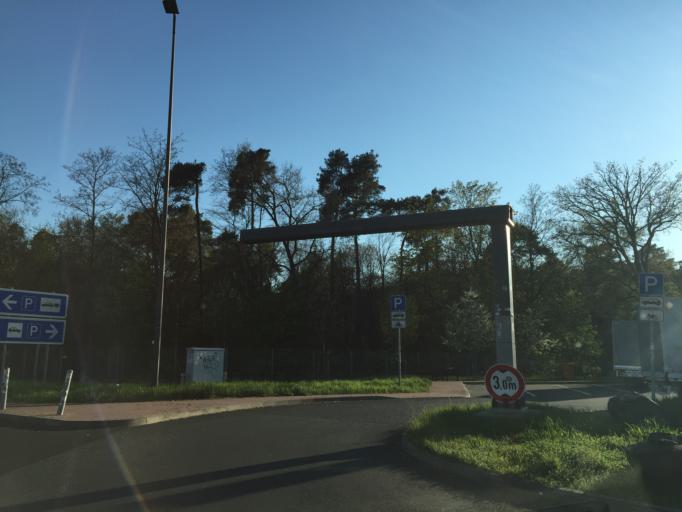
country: DE
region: Hesse
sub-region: Regierungsbezirk Darmstadt
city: Erzhausen
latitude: 49.9465
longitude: 8.6091
